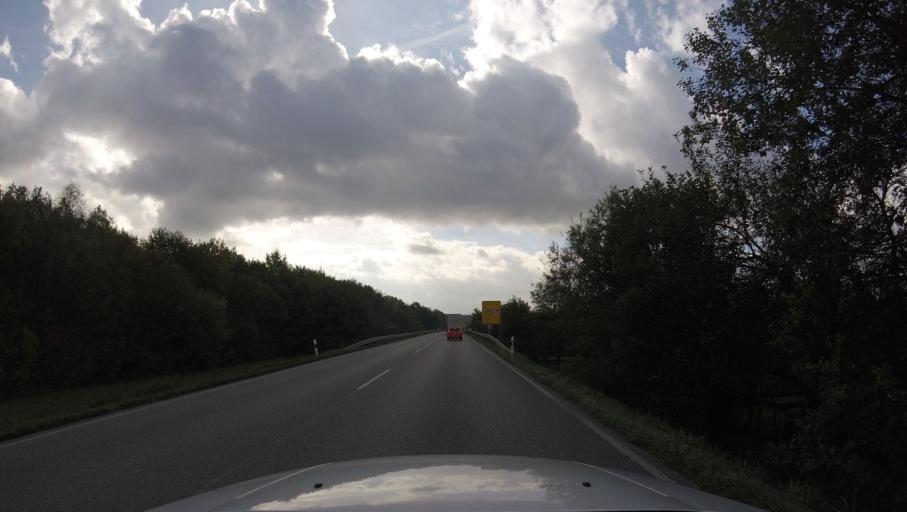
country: DE
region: Baden-Wuerttemberg
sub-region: Regierungsbezirk Stuttgart
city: Aspach
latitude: 48.9548
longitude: 9.4173
